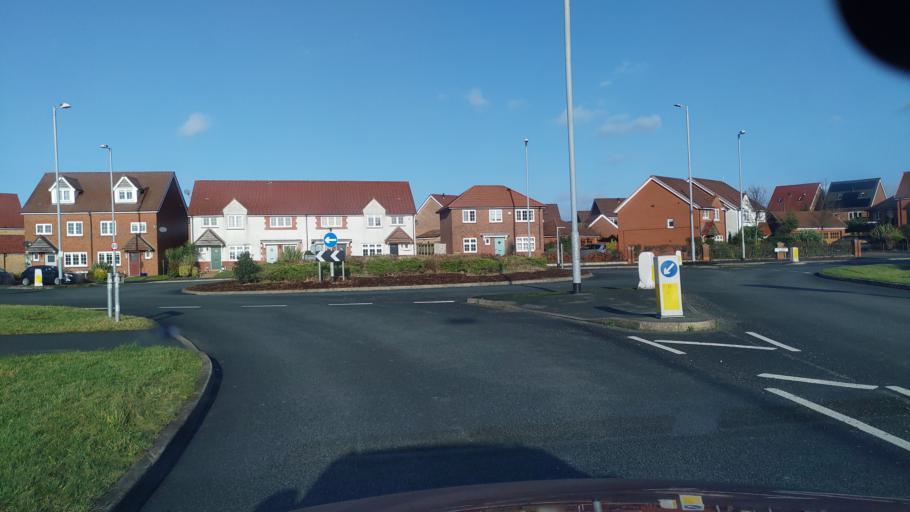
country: GB
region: England
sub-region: Lancashire
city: Clayton-le-Woods
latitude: 53.6792
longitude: -2.6571
